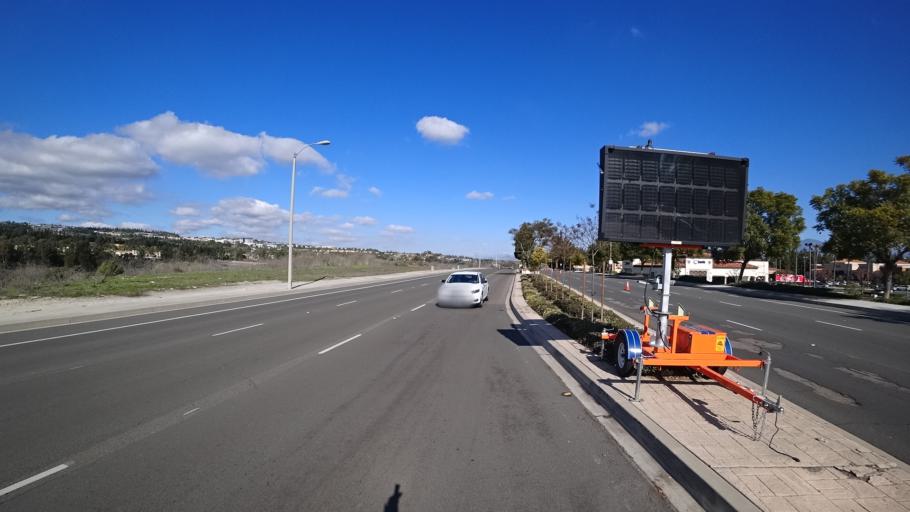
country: US
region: California
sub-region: Orange County
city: Aliso Viejo
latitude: 33.5680
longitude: -117.7151
